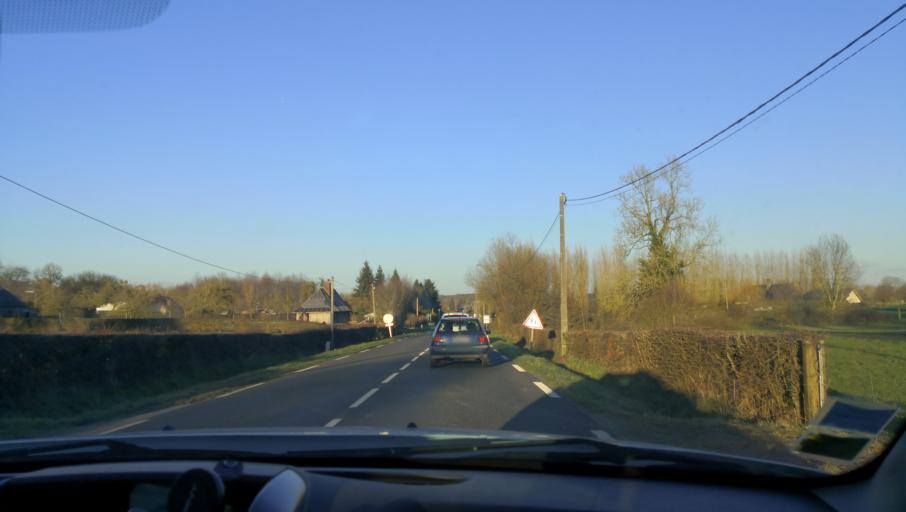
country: FR
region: Haute-Normandie
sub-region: Departement de la Seine-Maritime
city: Forges-les-Eaux
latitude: 49.6015
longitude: 1.4793
